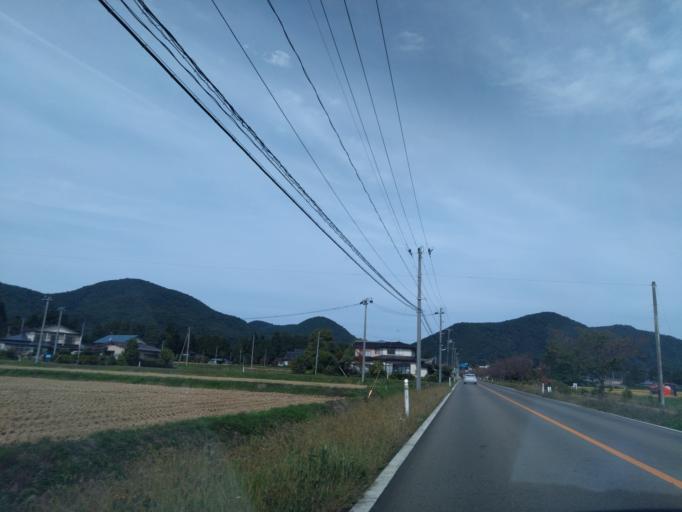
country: JP
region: Iwate
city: Hanamaki
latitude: 39.4410
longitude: 141.0774
